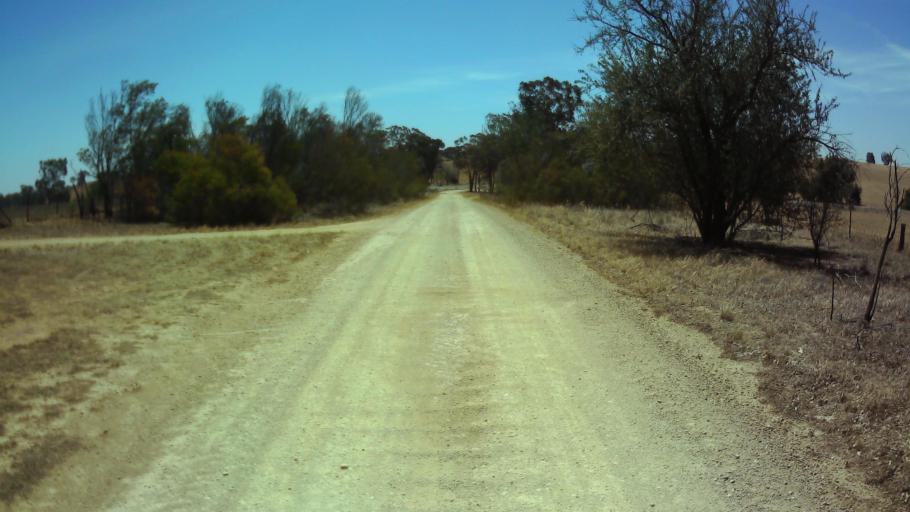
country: AU
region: New South Wales
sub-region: Weddin
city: Grenfell
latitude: -33.9256
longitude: 148.1780
